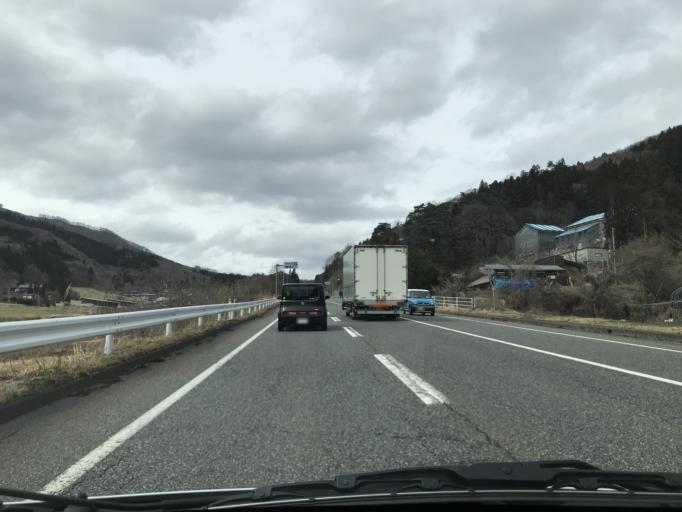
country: JP
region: Iwate
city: Tono
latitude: 39.3389
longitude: 141.4426
